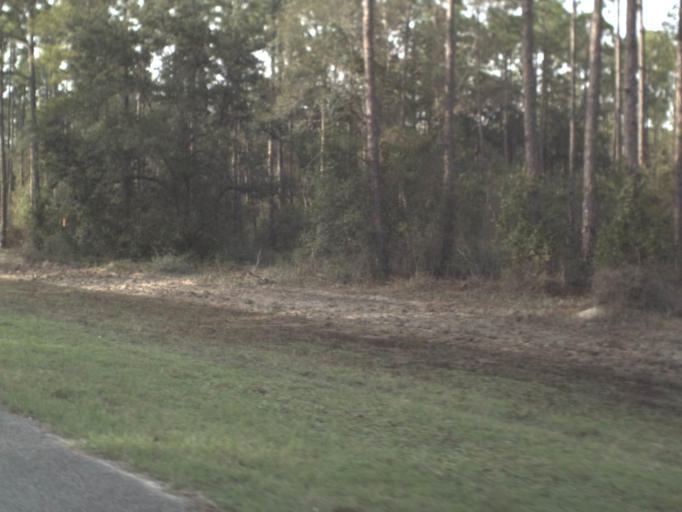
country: US
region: Florida
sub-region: Bay County
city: Mexico Beach
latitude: 29.9678
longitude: -85.4519
